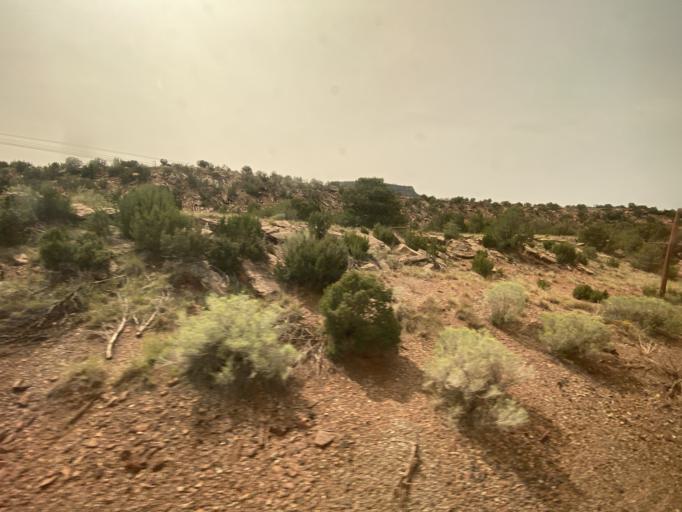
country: US
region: New Mexico
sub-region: San Miguel County
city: Pecos
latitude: 35.3983
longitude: -105.4935
